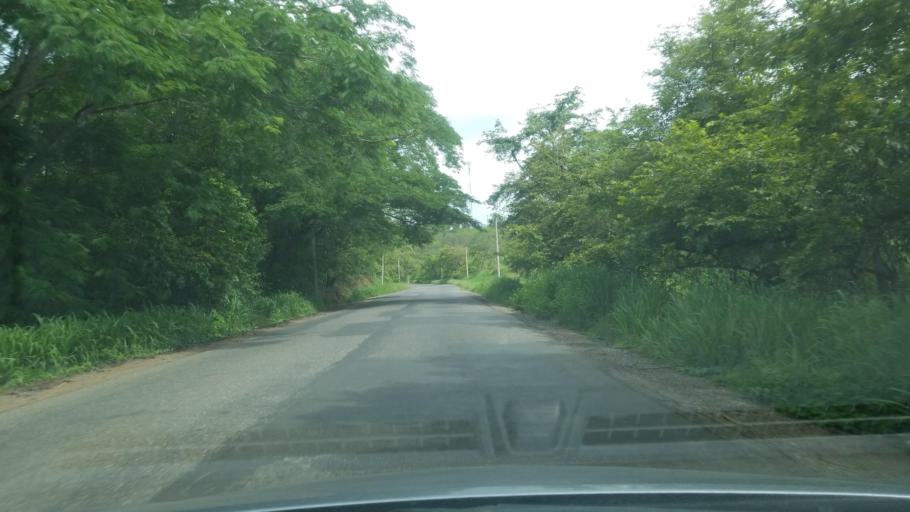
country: HN
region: Santa Barbara
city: Camalote
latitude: 15.3392
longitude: -88.3570
